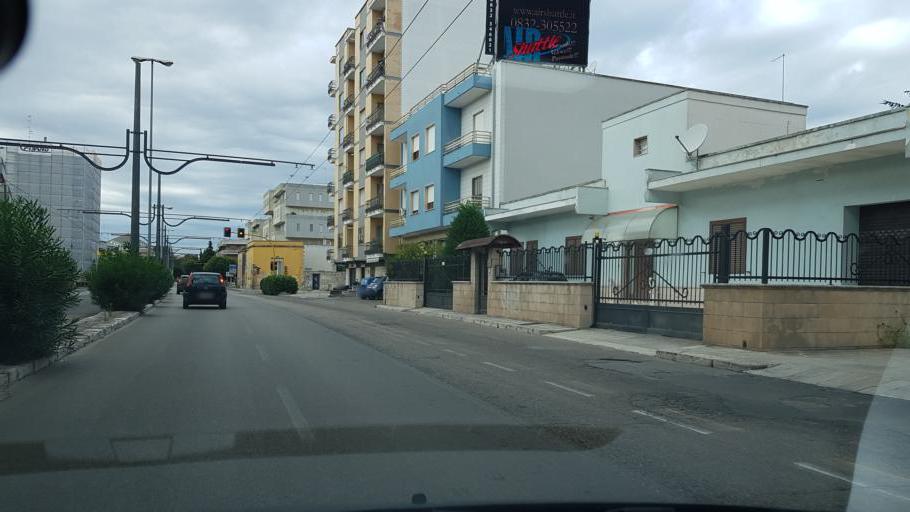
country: IT
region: Apulia
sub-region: Provincia di Lecce
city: Lecce
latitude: 40.3620
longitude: 18.1781
